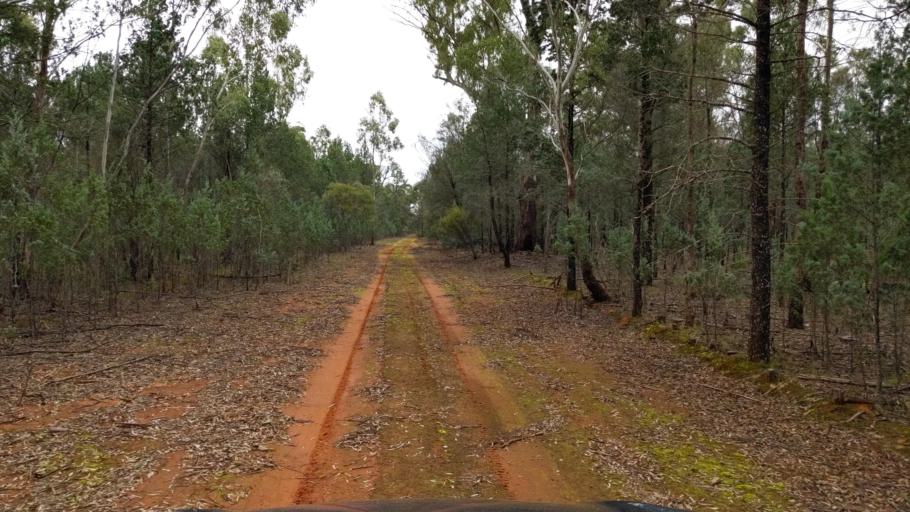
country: AU
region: New South Wales
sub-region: Coolamon
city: Coolamon
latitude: -34.8373
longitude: 146.9343
